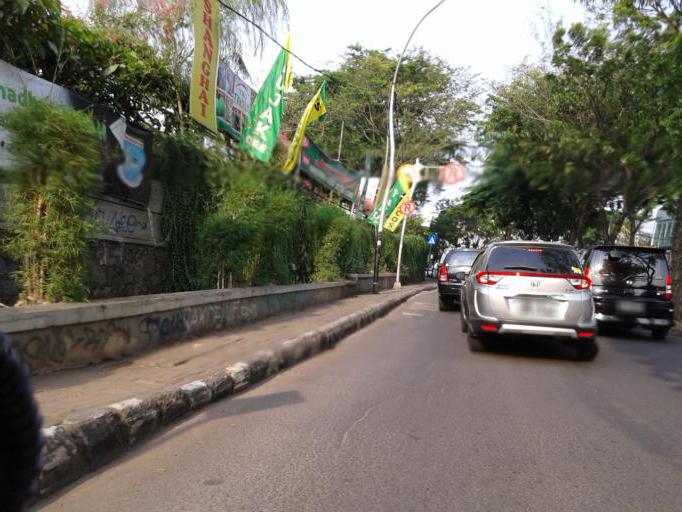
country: ID
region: Banten
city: South Tangerang
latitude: -6.2800
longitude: 106.7164
